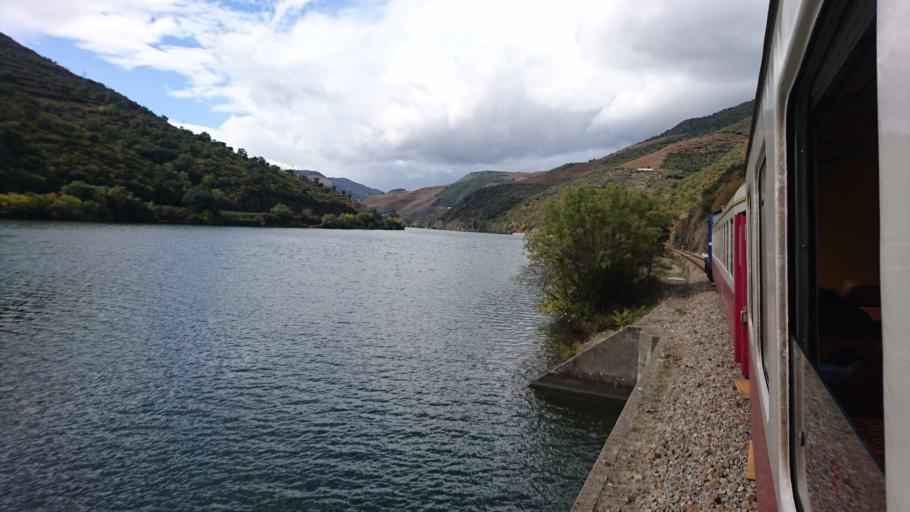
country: PT
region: Viseu
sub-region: Armamar
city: Armamar
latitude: 41.1636
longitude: -7.6580
